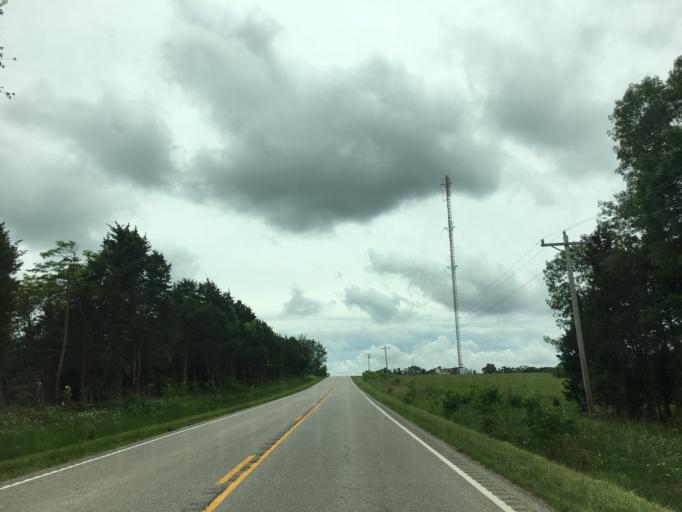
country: US
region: Missouri
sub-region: Gasconade County
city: Owensville
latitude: 38.4920
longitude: -91.4620
